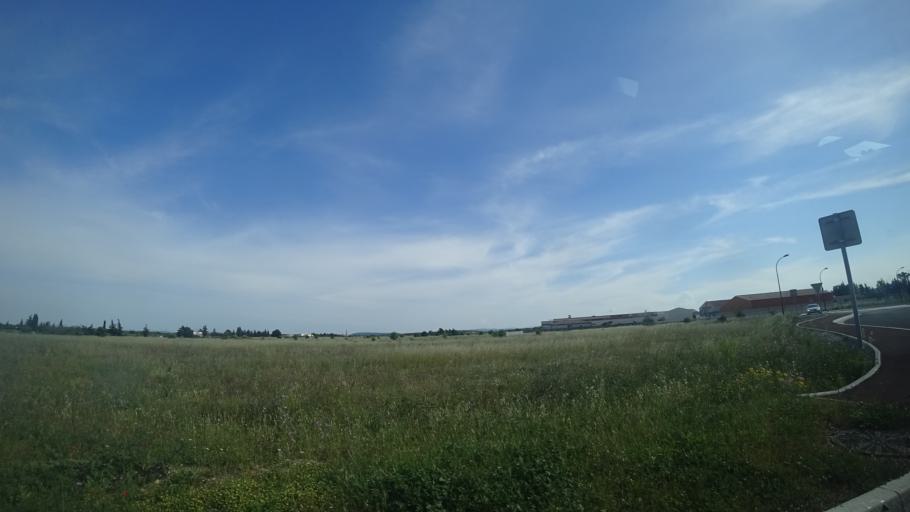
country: FR
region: Languedoc-Roussillon
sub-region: Departement de l'Aude
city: Argeliers
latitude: 43.3043
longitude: 2.9036
